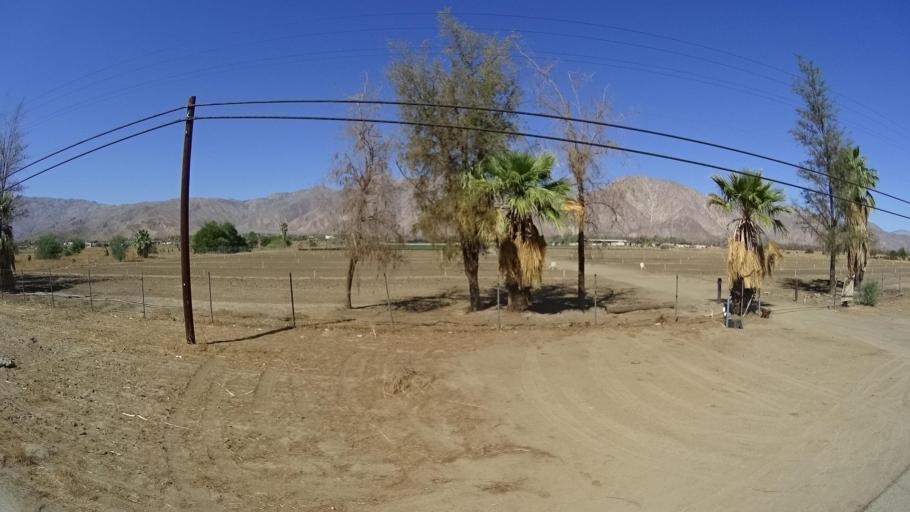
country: US
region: California
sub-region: San Diego County
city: Borrego Springs
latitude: 33.2677
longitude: -116.3661
